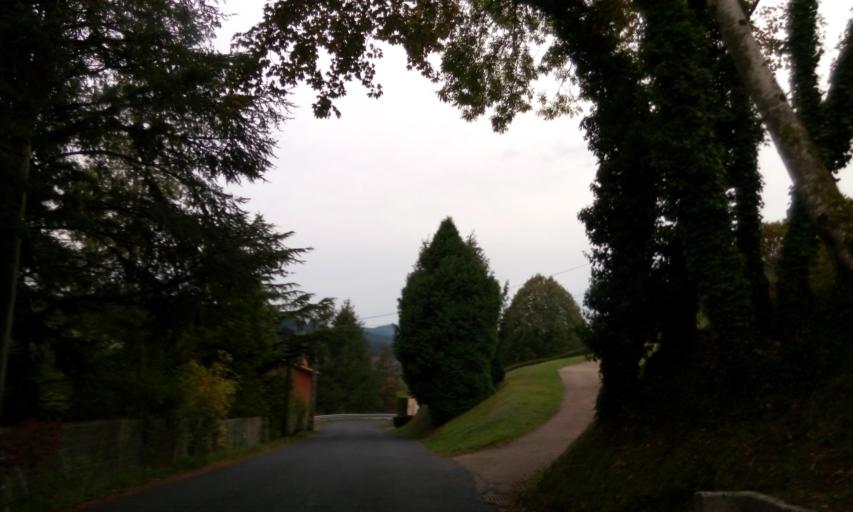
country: FR
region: Rhone-Alpes
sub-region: Departement du Rhone
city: Cublize
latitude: 46.0749
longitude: 4.3906
